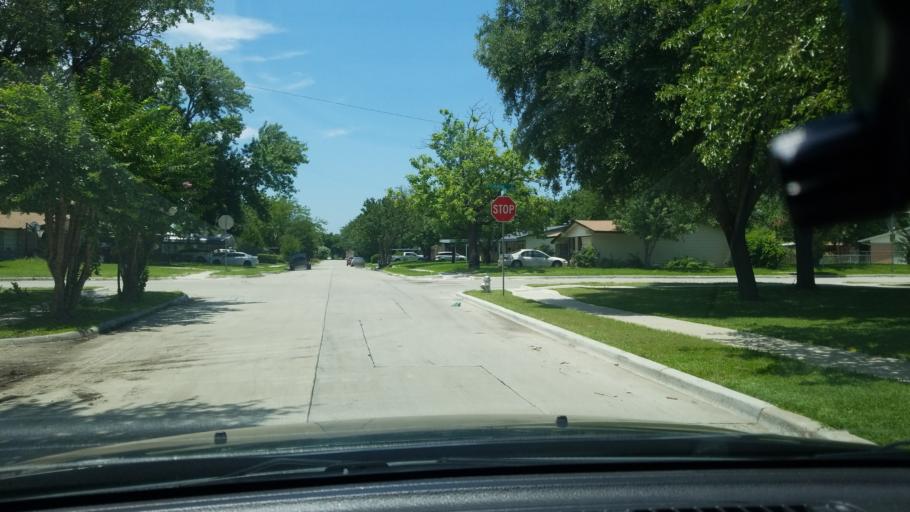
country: US
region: Texas
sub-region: Dallas County
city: Mesquite
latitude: 32.8022
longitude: -96.6531
